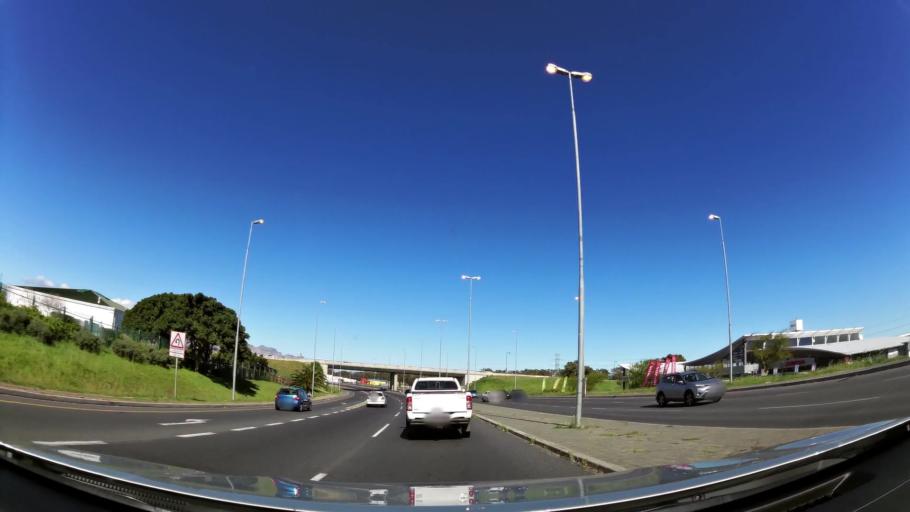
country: ZA
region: Western Cape
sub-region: Cape Winelands District Municipality
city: Stellenbosch
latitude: -34.0804
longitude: 18.8191
